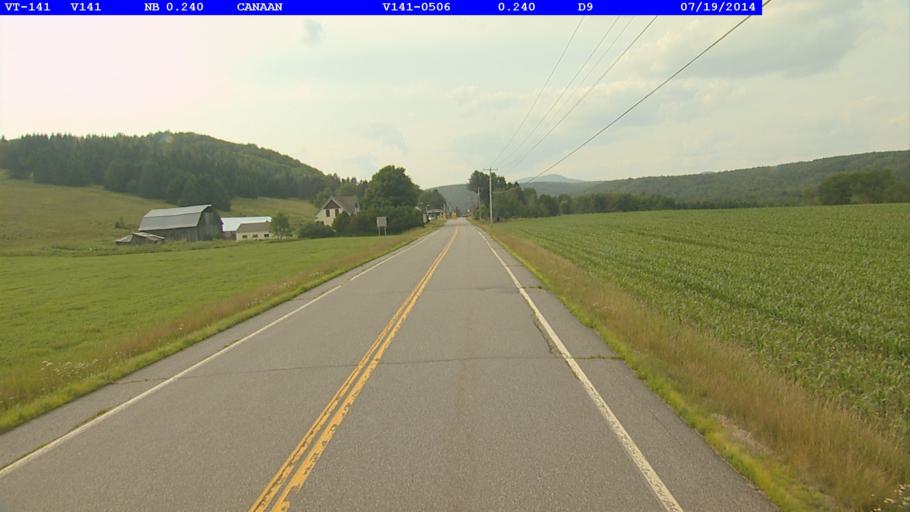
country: US
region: New Hampshire
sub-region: Coos County
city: Colebrook
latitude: 45.0097
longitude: -71.5578
